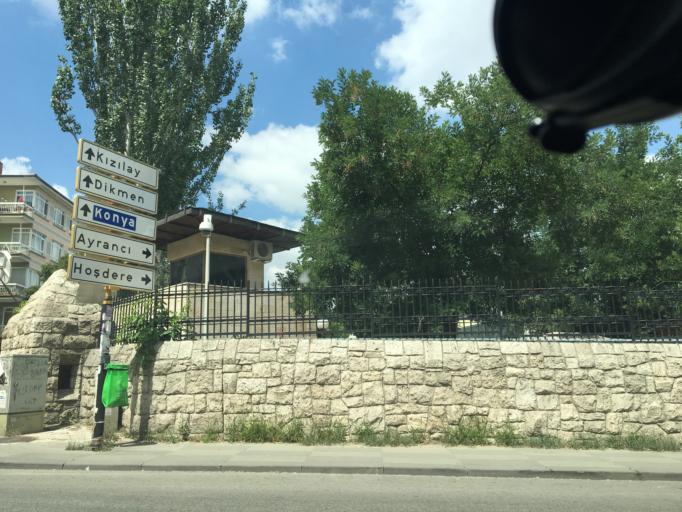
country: TR
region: Ankara
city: Ankara
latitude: 39.9054
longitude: 32.8531
